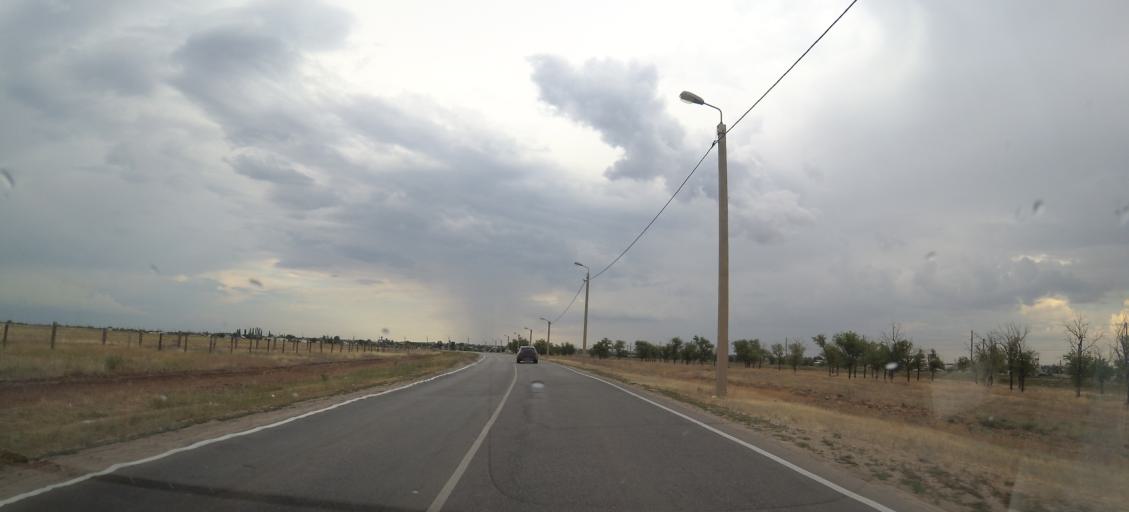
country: RU
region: Volgograd
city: Kotel'nikovo
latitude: 47.6150
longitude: 43.1272
